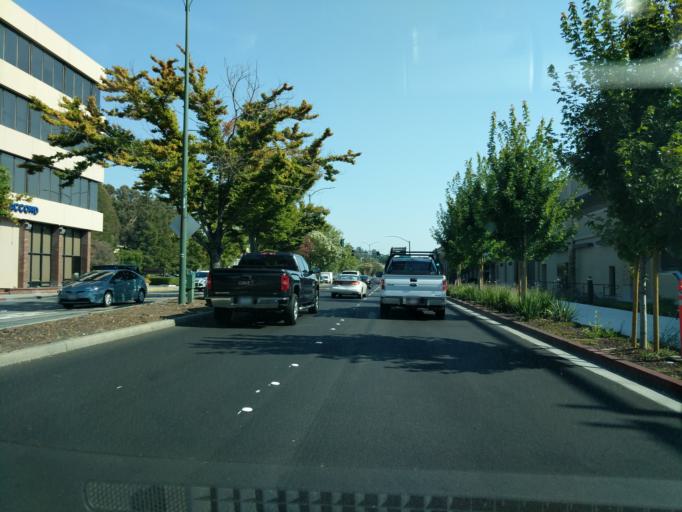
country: US
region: California
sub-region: Contra Costa County
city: Walnut Creek
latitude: 37.8964
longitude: -122.0567
